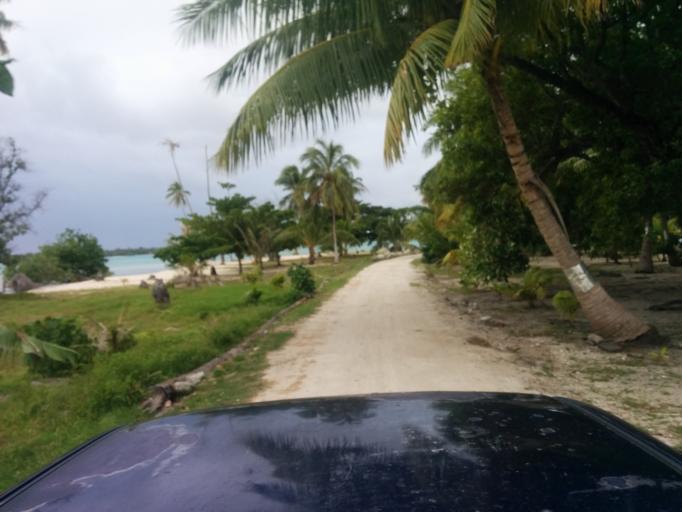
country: PF
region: Iles Sous-le-Vent
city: Vaitape
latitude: -16.4496
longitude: -152.2739
